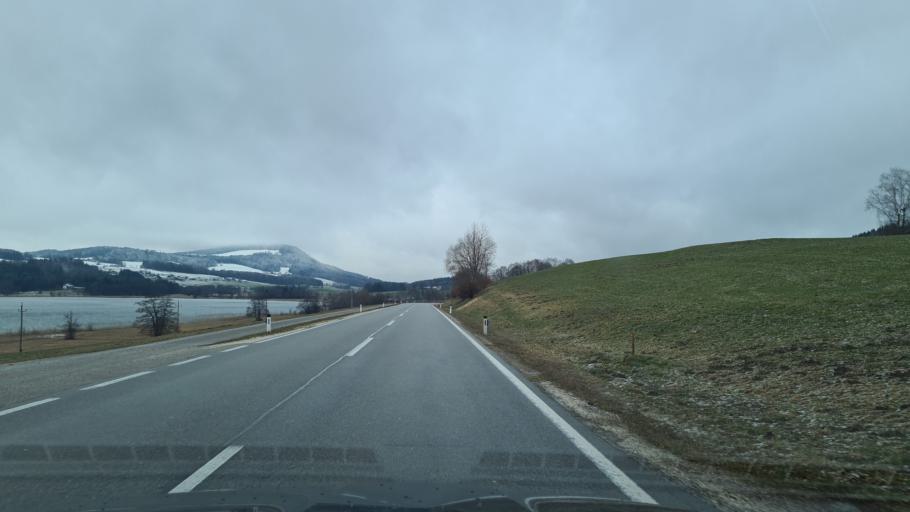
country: AT
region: Upper Austria
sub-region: Politischer Bezirk Vocklabruck
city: Zell am Moos
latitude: 47.9237
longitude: 13.3142
